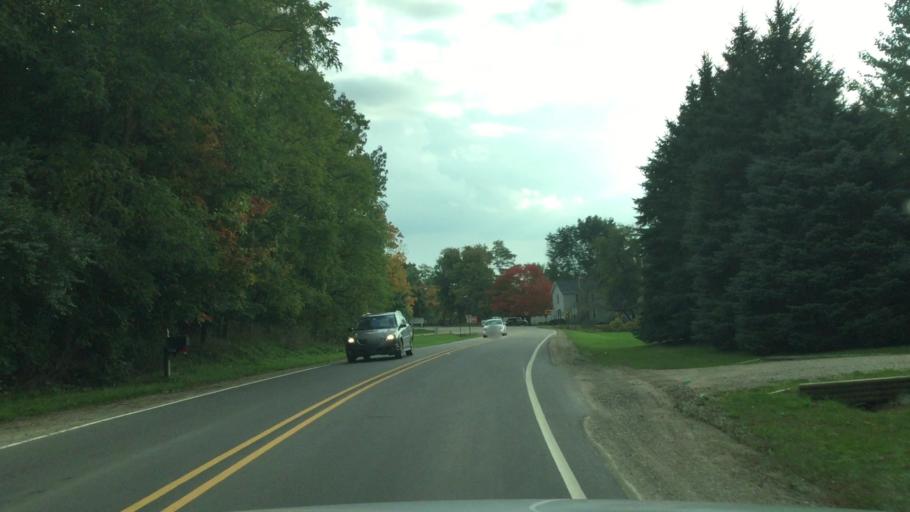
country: US
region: Michigan
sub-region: Genesee County
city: Fenton
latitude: 42.6961
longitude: -83.7028
